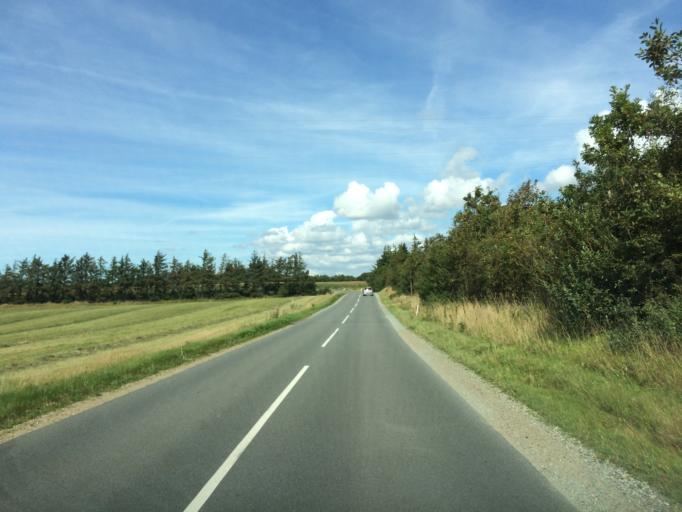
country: DK
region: South Denmark
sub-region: Varde Kommune
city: Oksbol
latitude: 55.7296
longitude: 8.2524
